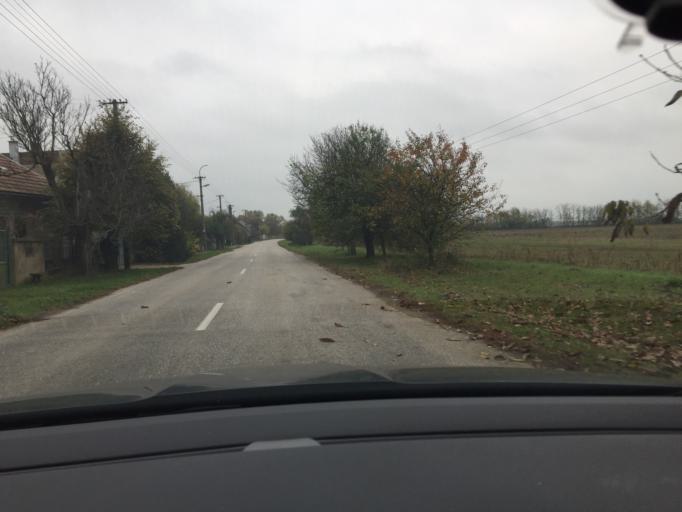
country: HU
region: Komarom-Esztergom
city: Esztergom
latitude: 47.9299
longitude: 18.7481
